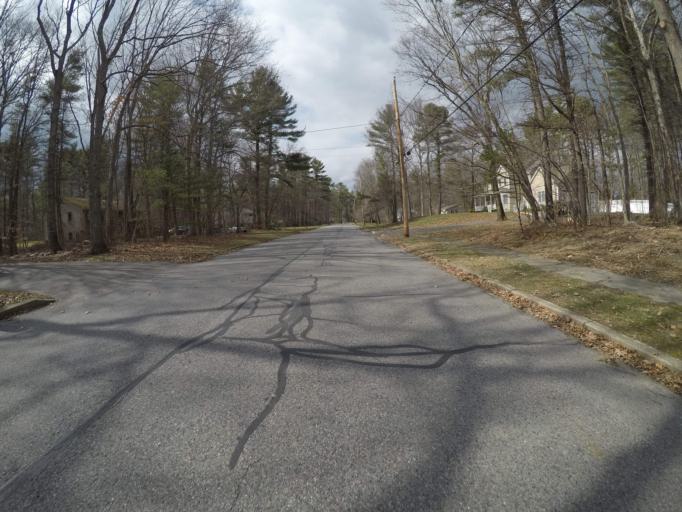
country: US
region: Massachusetts
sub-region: Bristol County
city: Easton
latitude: 42.0363
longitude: -71.1138
